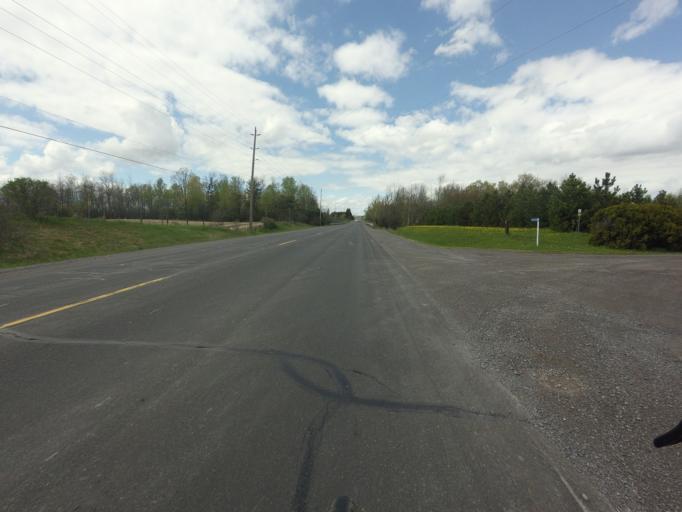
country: CA
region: Ontario
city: Carleton Place
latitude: 45.2444
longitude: -76.2356
